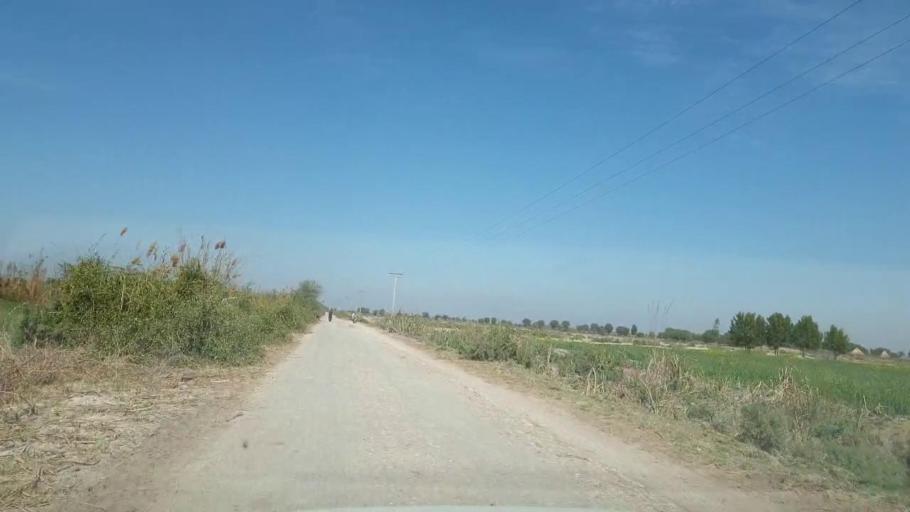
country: PK
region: Sindh
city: Pithoro
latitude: 25.6154
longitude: 69.2161
